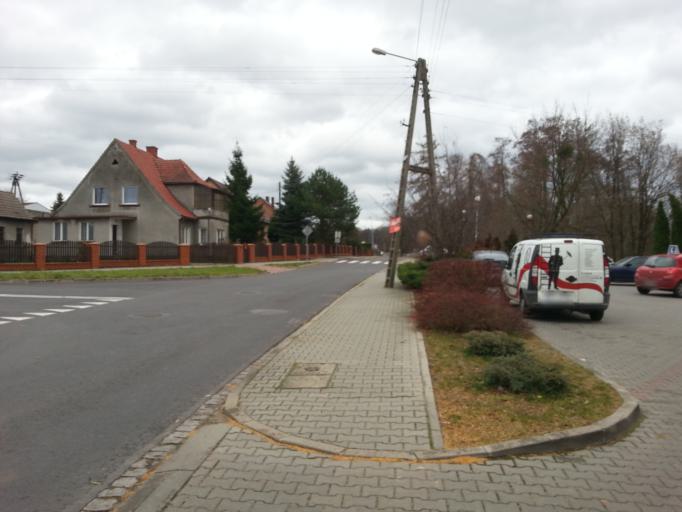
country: PL
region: Lower Silesian Voivodeship
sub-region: Powiat olesnicki
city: Twardogora
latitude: 51.3656
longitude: 17.4720
